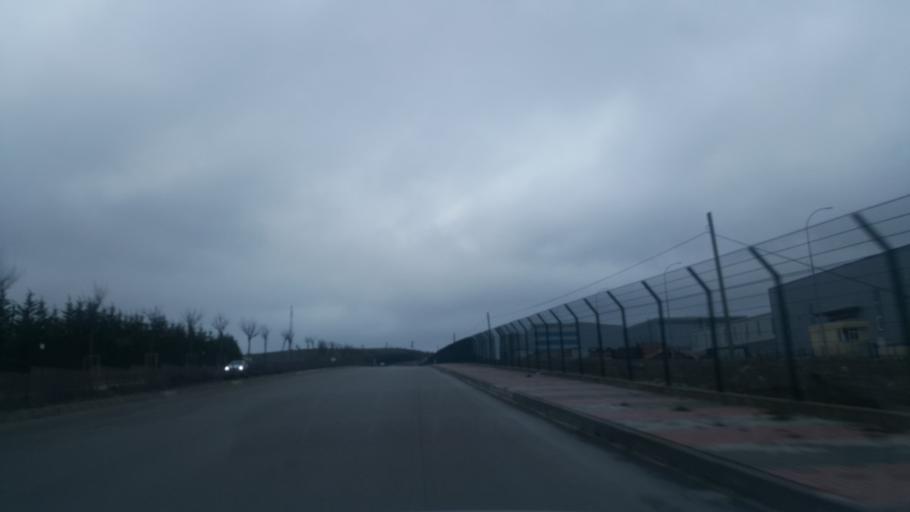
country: TR
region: Kocaeli
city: Tavsancil
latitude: 40.8177
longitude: 29.5648
